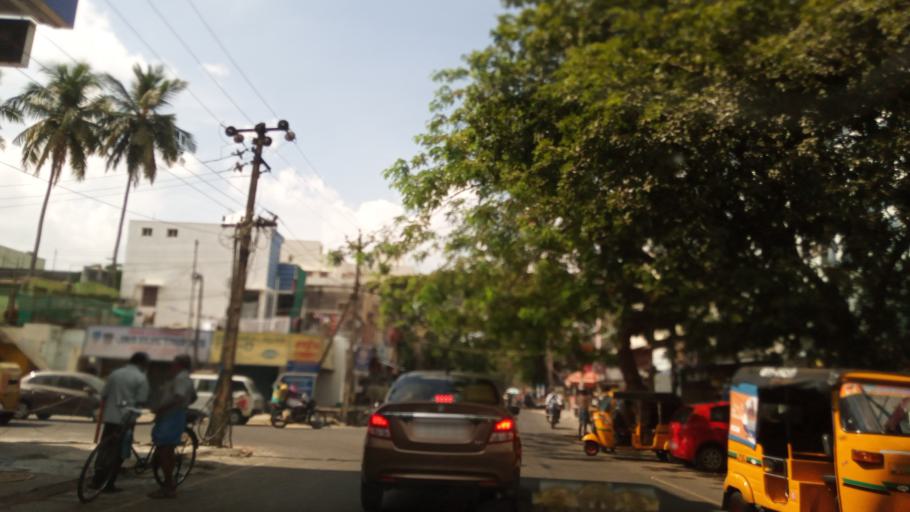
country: IN
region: Tamil Nadu
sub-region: Kancheepuram
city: Saint Thomas Mount
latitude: 12.9833
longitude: 80.1885
